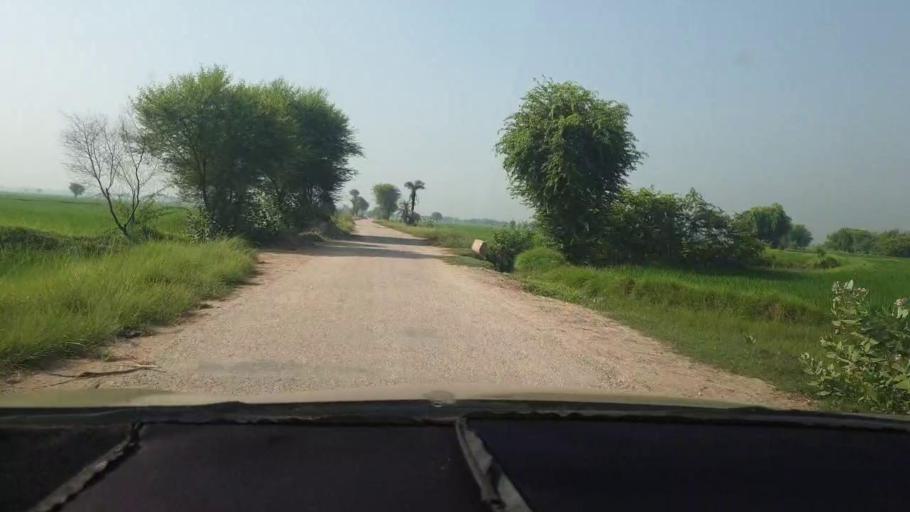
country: PK
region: Sindh
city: Kambar
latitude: 27.6318
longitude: 68.0899
